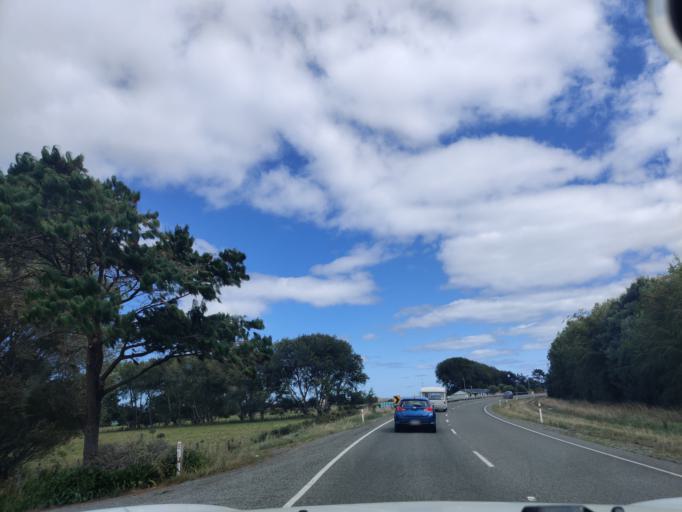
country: NZ
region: Manawatu-Wanganui
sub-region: Horowhenua District
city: Foxton
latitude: -40.4199
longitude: 175.4133
